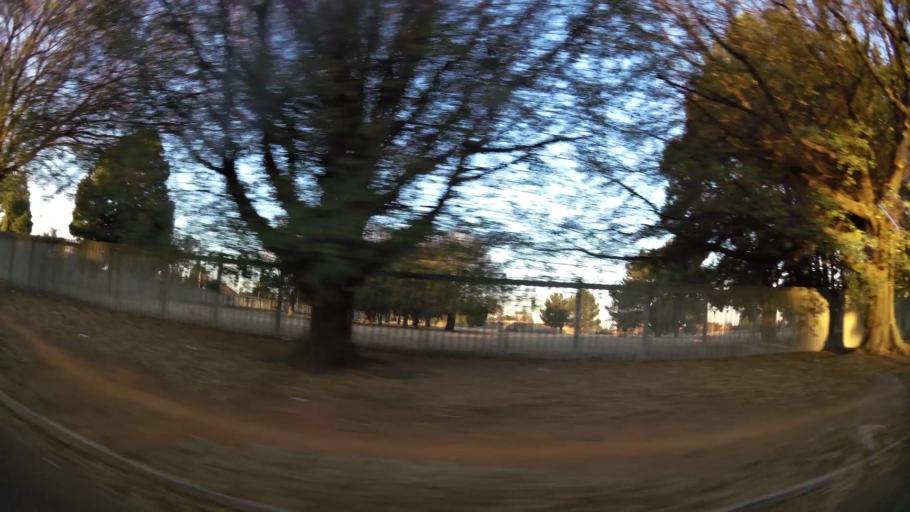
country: ZA
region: Gauteng
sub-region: City of Johannesburg Metropolitan Municipality
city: Roodepoort
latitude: -26.1485
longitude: 27.8820
